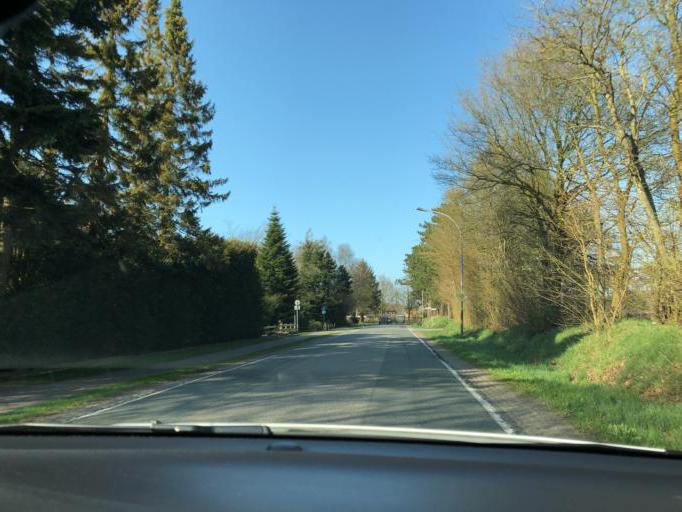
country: DE
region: Schleswig-Holstein
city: Bargum
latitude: 54.6887
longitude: 8.9639
